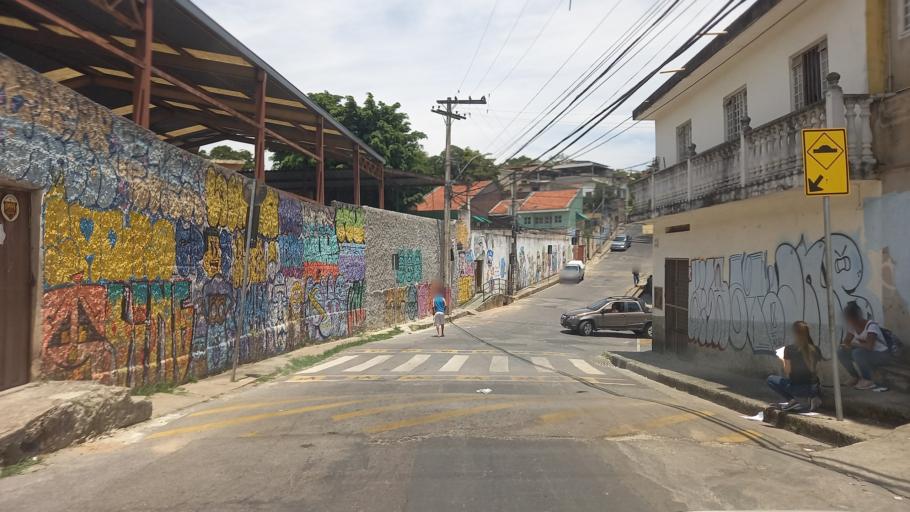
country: BR
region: Minas Gerais
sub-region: Contagem
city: Contagem
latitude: -19.9102
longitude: -44.0086
